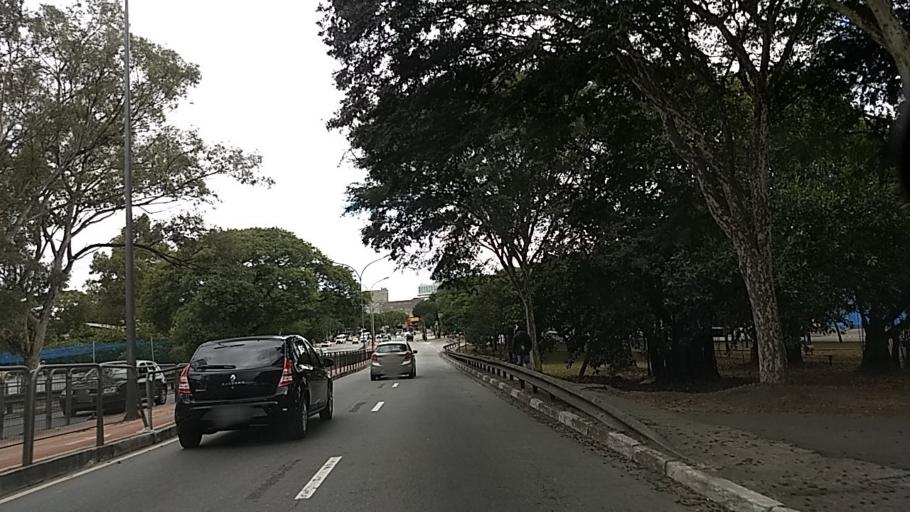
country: BR
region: Sao Paulo
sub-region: Sao Paulo
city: Sao Paulo
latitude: -23.5243
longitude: -46.6114
